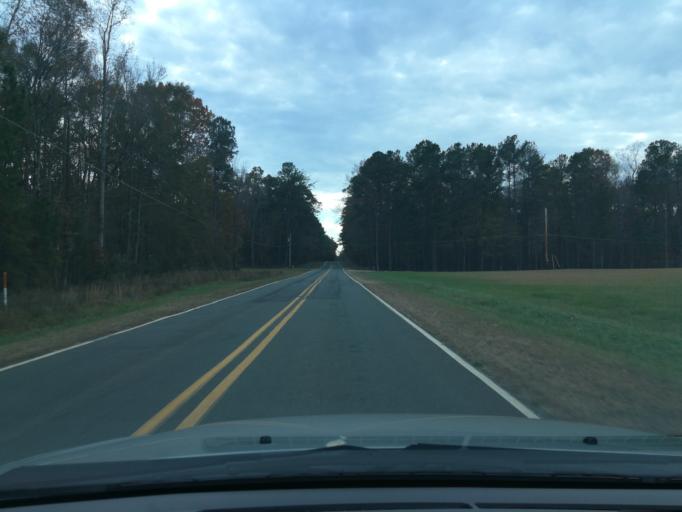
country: US
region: North Carolina
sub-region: Orange County
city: Hillsborough
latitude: 36.0148
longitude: -79.0419
